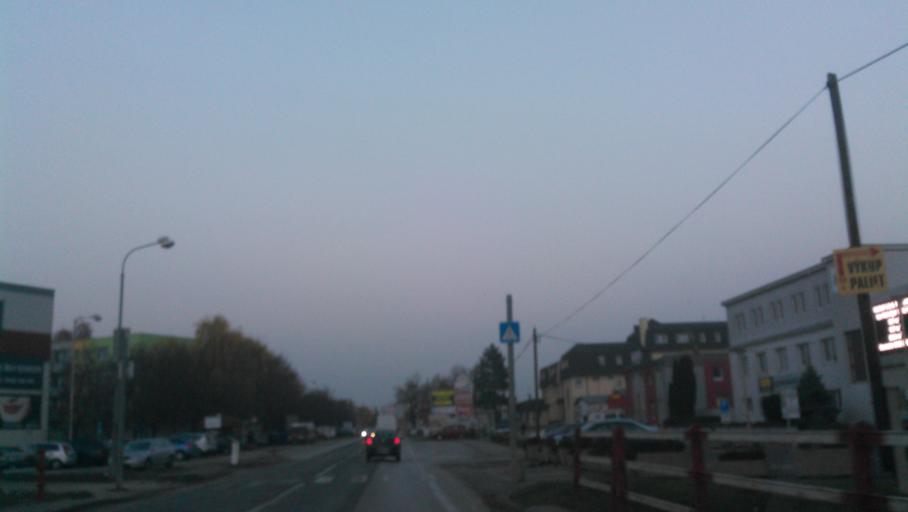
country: SK
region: Bratislavsky
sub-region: Okres Pezinok
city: Pezinok
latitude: 48.2784
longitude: 17.2579
